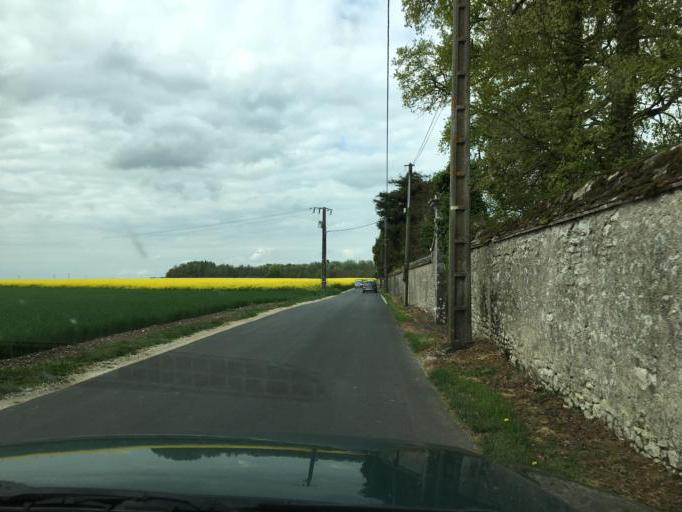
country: FR
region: Centre
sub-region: Departement du Loiret
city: Meung-sur-Loire
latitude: 47.8626
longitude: 1.6870
